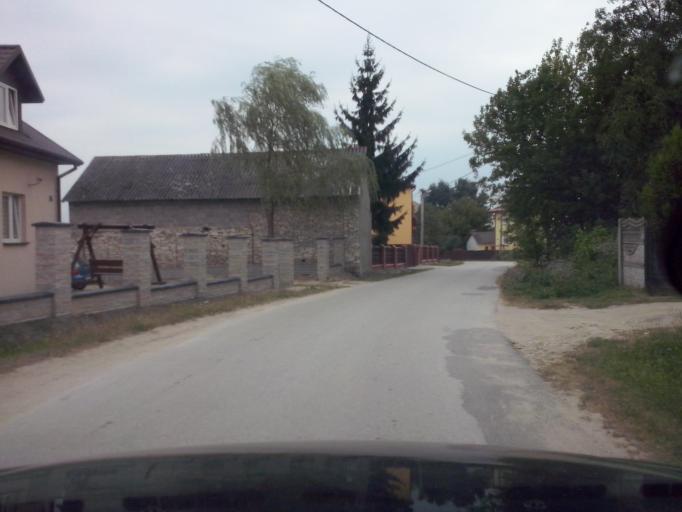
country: PL
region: Swietokrzyskie
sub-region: Powiat kielecki
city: Morawica
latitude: 50.6936
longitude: 20.5713
